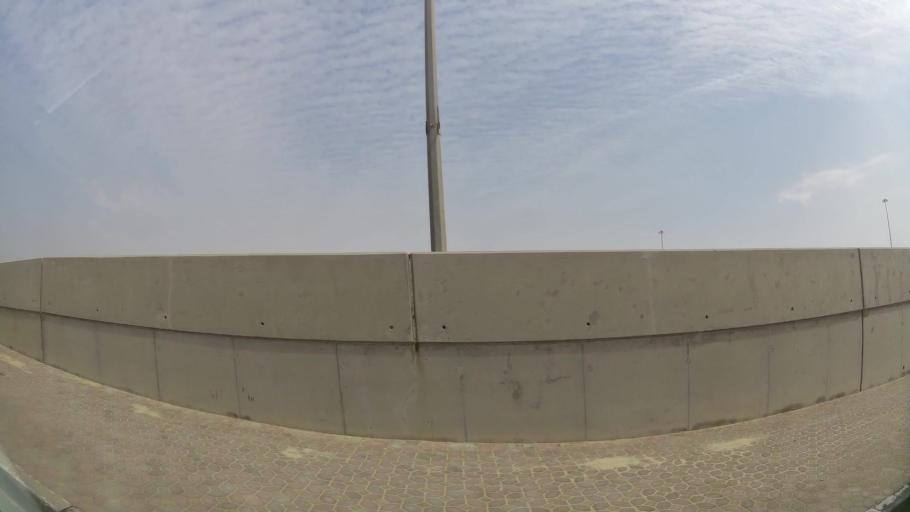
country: AE
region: Abu Dhabi
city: Abu Dhabi
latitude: 24.5398
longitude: 54.6839
